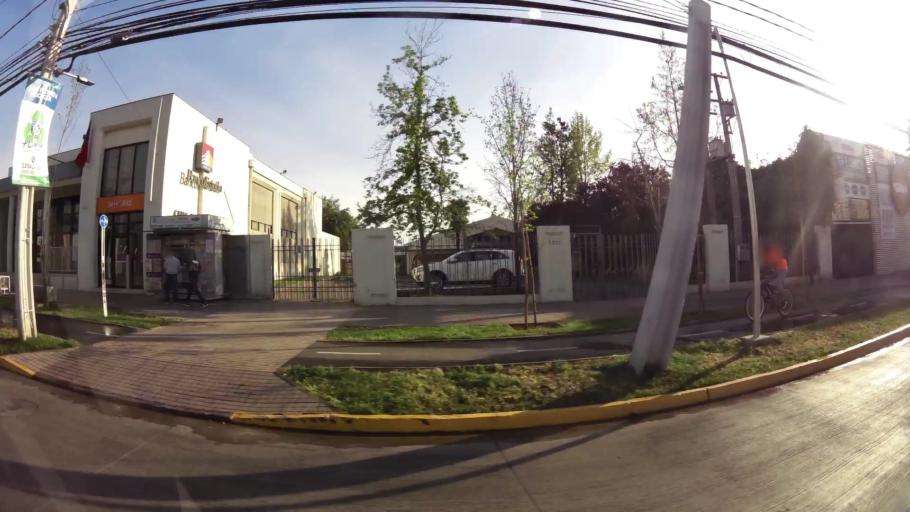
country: CL
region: Santiago Metropolitan
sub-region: Provincia de Santiago
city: Villa Presidente Frei, Nunoa, Santiago, Chile
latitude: -33.5218
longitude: -70.6004
